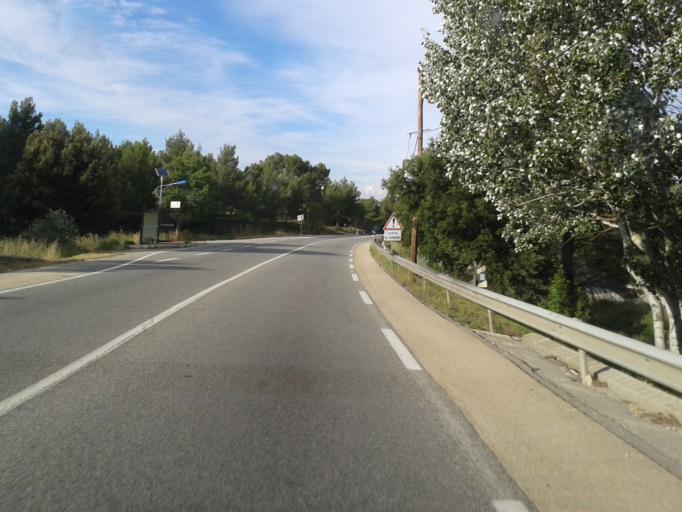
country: FR
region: Provence-Alpes-Cote d'Azur
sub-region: Departement des Bouches-du-Rhone
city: Meyrargues
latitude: 43.6294
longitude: 5.5108
